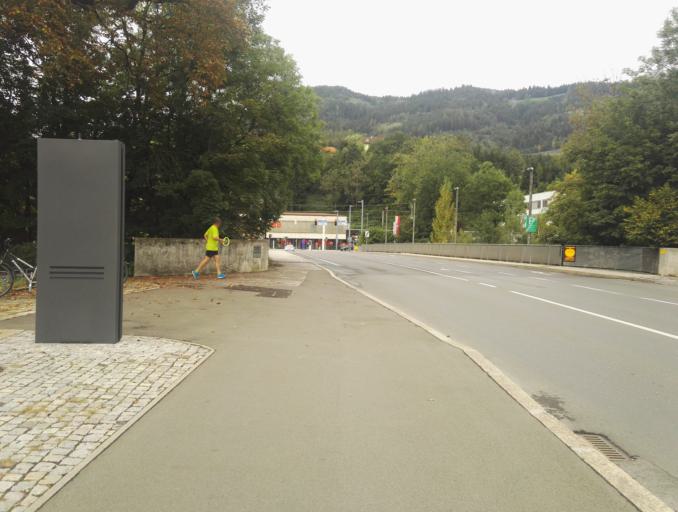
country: AT
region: Styria
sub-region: Politischer Bezirk Leoben
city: Leoben
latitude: 47.3859
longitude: 15.0917
